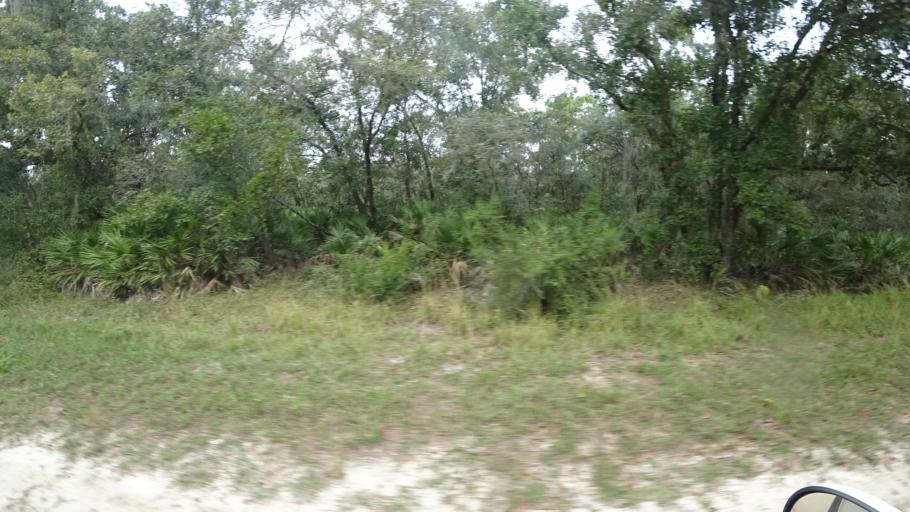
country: US
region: Florida
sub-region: Hillsborough County
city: Wimauma
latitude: 27.6291
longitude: -82.2797
